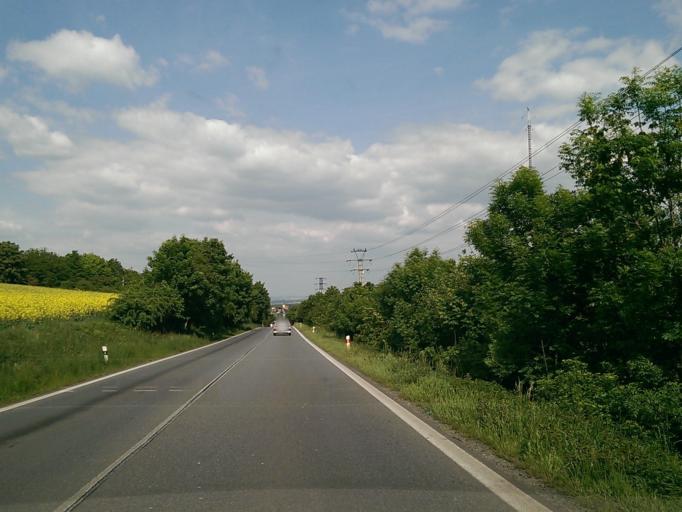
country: CZ
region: Central Bohemia
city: Zdiby
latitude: 50.1805
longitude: 14.4639
